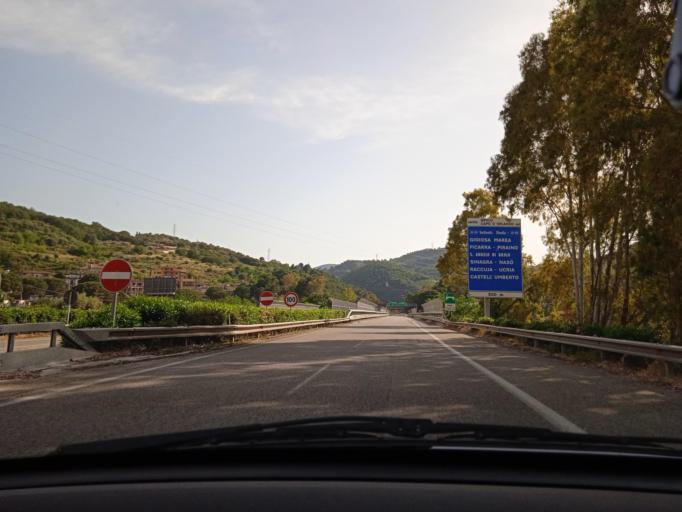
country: IT
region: Sicily
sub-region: Messina
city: Brolo
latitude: 38.1512
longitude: 14.8323
